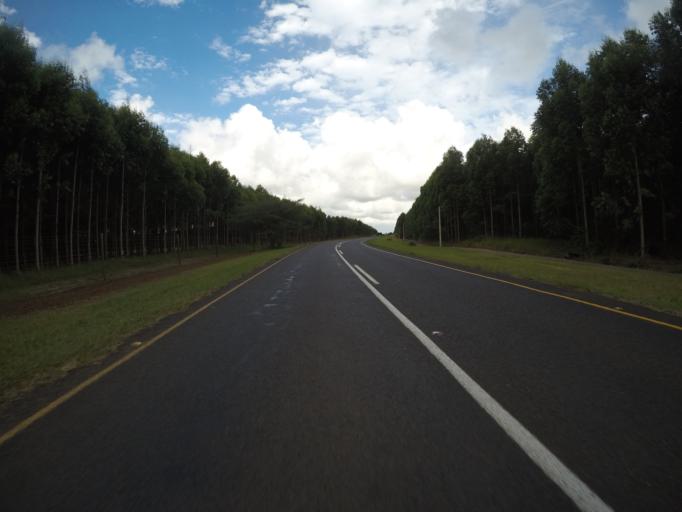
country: ZA
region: KwaZulu-Natal
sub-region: uMkhanyakude District Municipality
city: Mtubatuba
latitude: -28.3672
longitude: 32.2687
